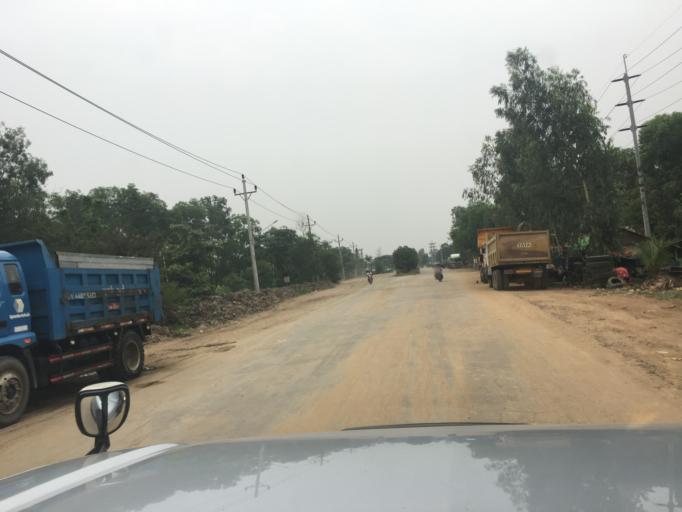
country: MM
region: Yangon
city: Syriam
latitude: 16.9477
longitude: 96.2806
